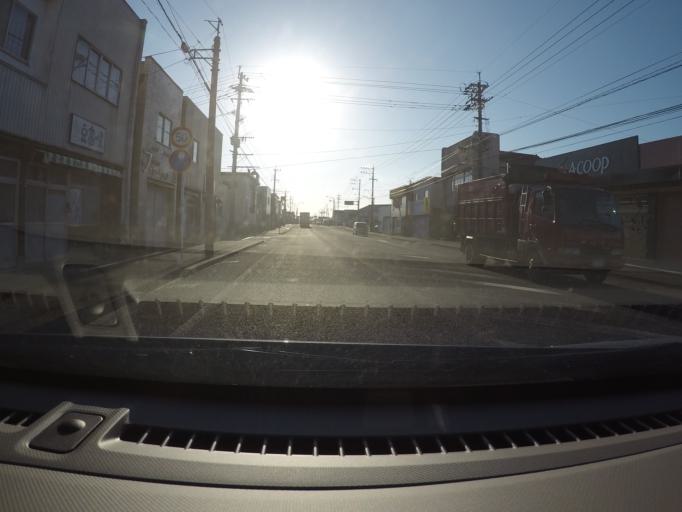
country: JP
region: Kagoshima
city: Izumi
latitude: 32.1145
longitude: 130.3351
